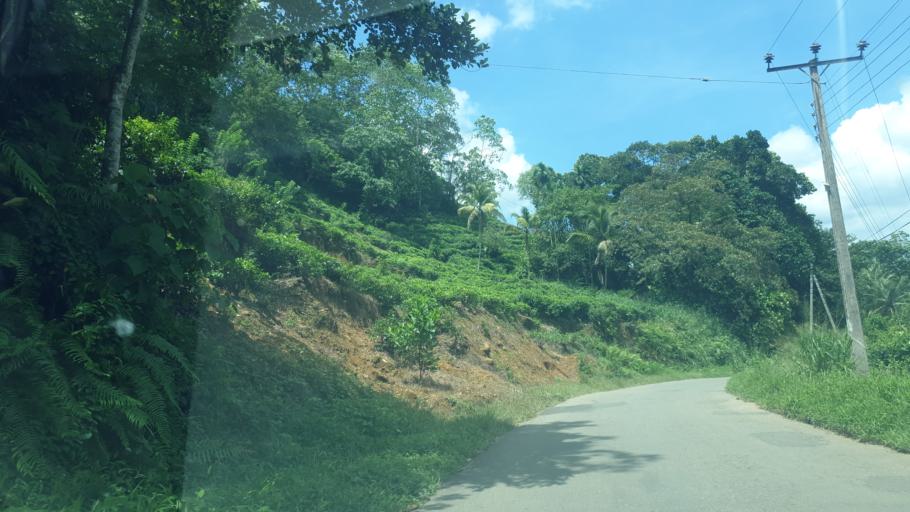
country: LK
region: Sabaragamuwa
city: Ratnapura
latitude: 6.4703
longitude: 80.4252
